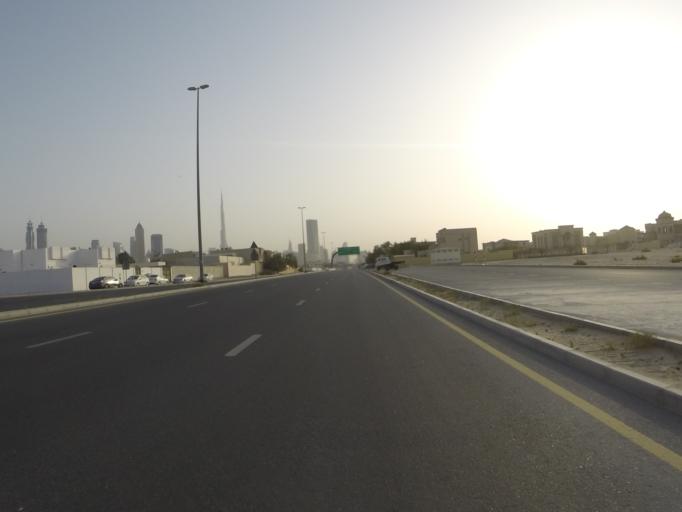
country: AE
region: Dubai
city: Dubai
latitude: 25.1631
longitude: 55.2574
